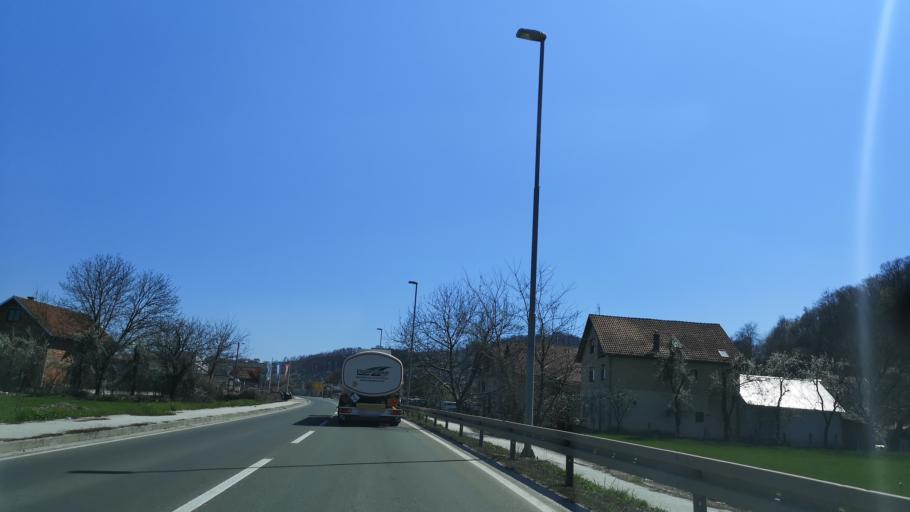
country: RS
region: Central Serbia
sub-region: Moravicki Okrug
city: Cacak
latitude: 43.8866
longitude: 20.3162
